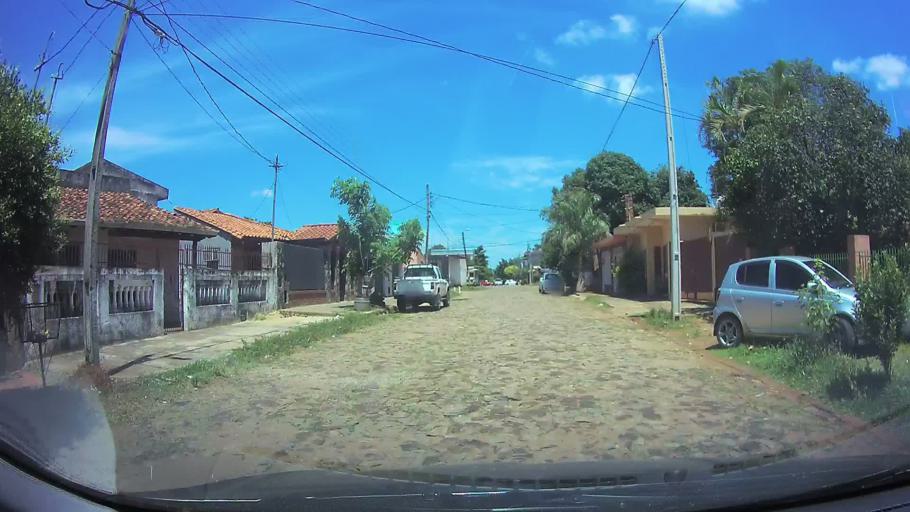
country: PY
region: Central
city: San Lorenzo
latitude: -25.2618
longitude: -57.4879
